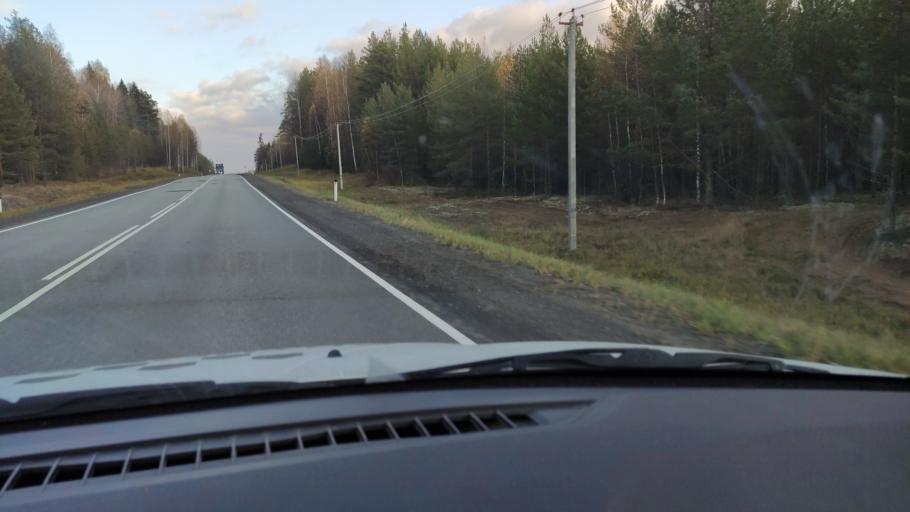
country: RU
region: Kirov
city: Belaya Kholunitsa
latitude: 58.9062
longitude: 51.0218
